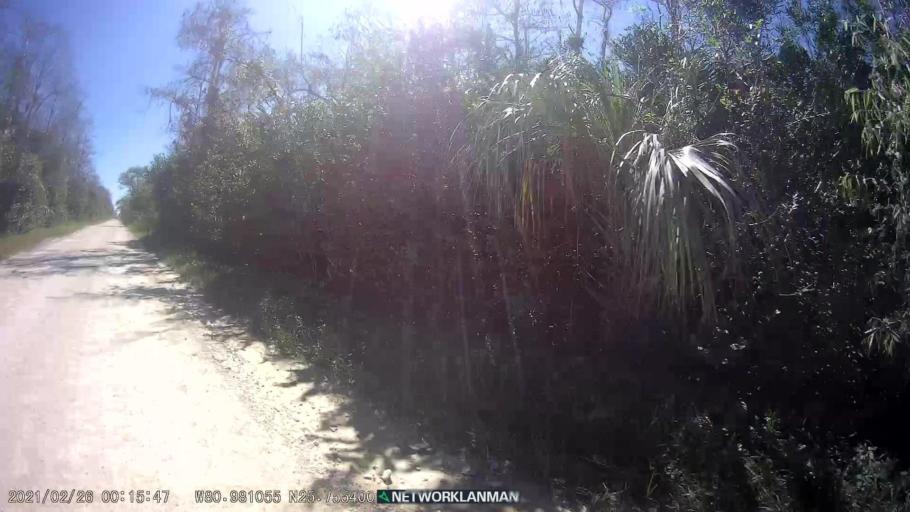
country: US
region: Florida
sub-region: Miami-Dade County
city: The Hammocks
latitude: 25.7552
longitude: -80.9804
